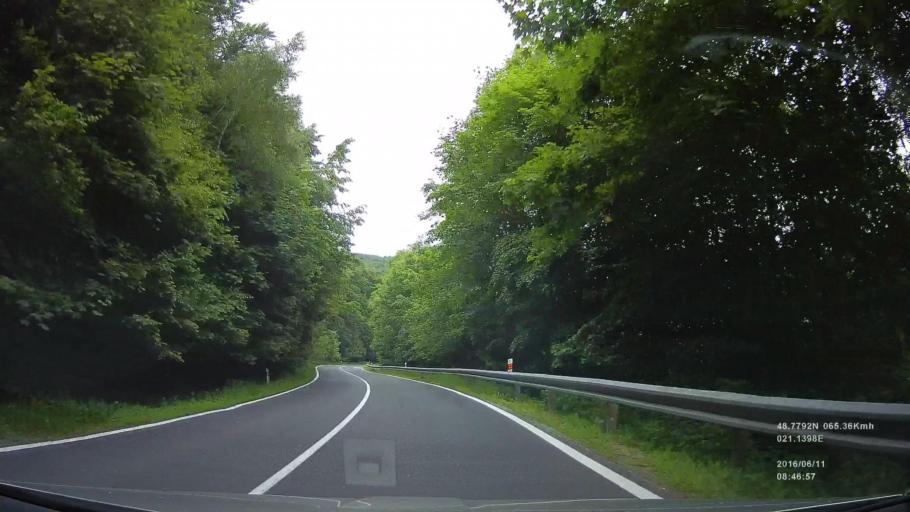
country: SK
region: Kosicky
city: Kosice
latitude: 48.7797
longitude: 21.1430
